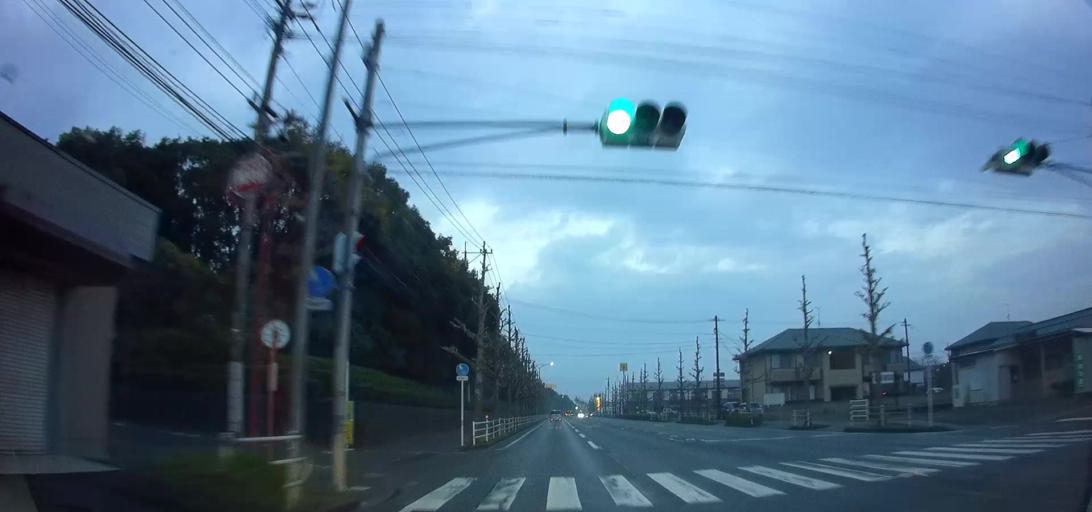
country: JP
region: Nagasaki
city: Omura
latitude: 32.9159
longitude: 129.9447
